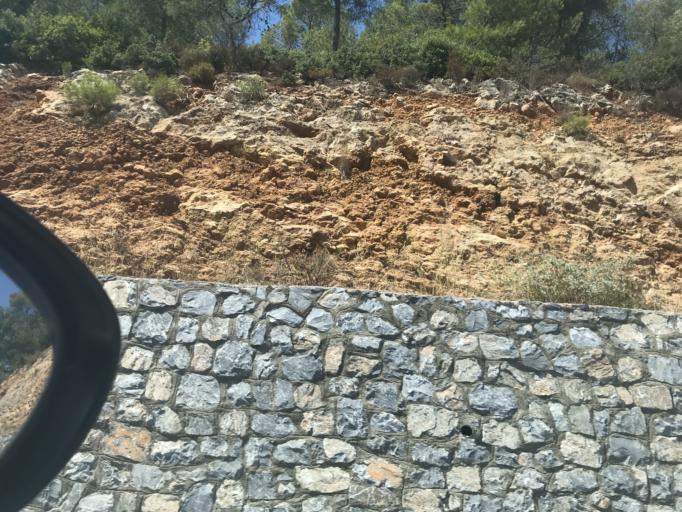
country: TR
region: Mugla
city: Kiulukioi
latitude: 37.1547
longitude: 27.5860
